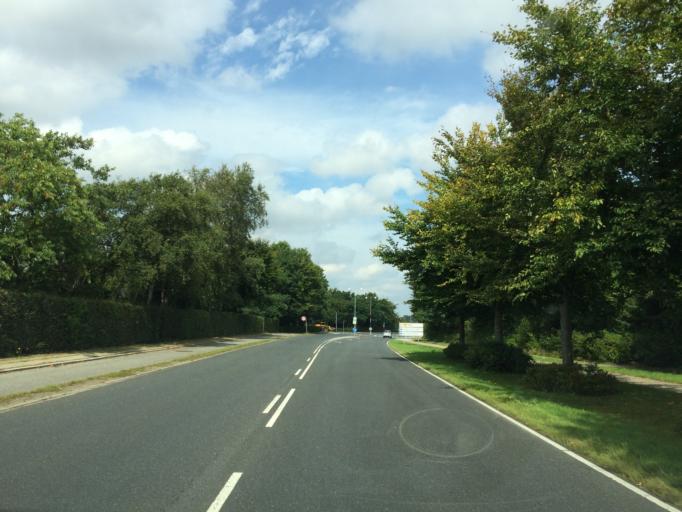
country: DK
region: Central Jutland
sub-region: Holstebro Kommune
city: Holstebro
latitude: 56.3724
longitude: 8.6112
